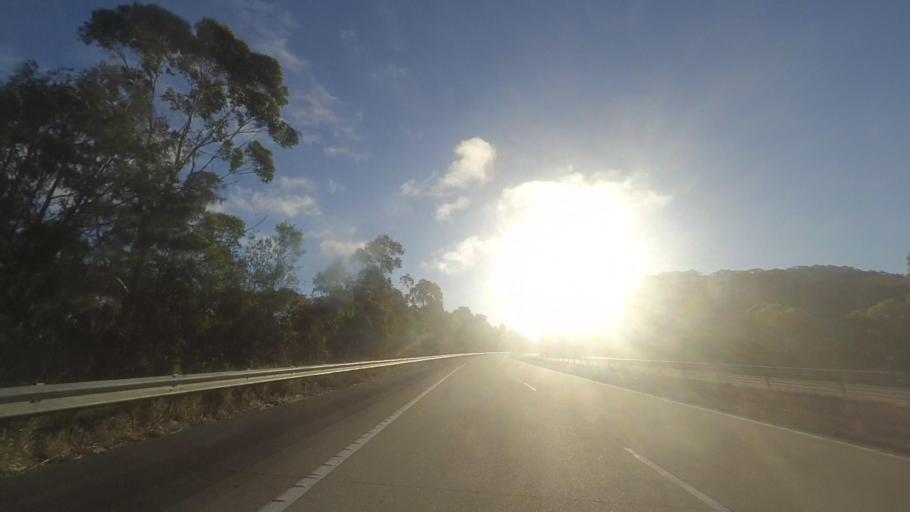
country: AU
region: New South Wales
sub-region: Great Lakes
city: Bulahdelah
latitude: -32.3860
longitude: 152.2599
